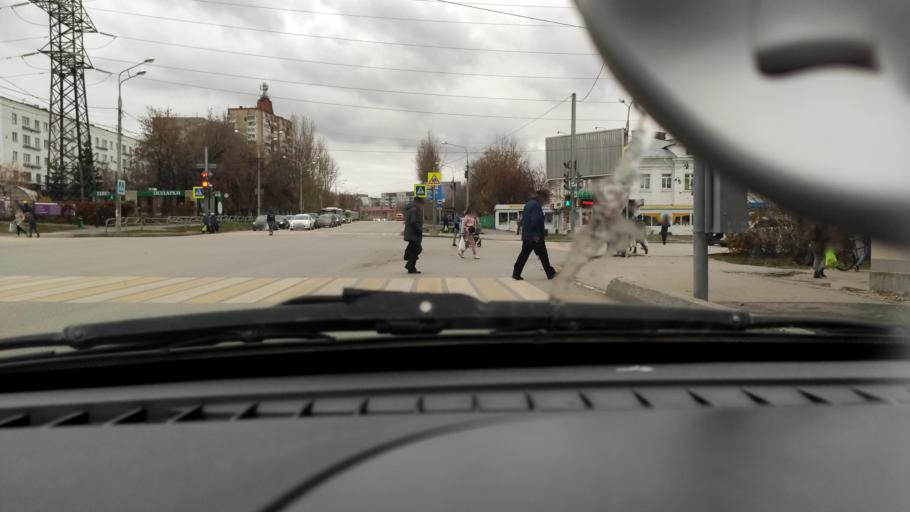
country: RU
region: Perm
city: Perm
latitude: 57.9807
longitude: 56.2158
